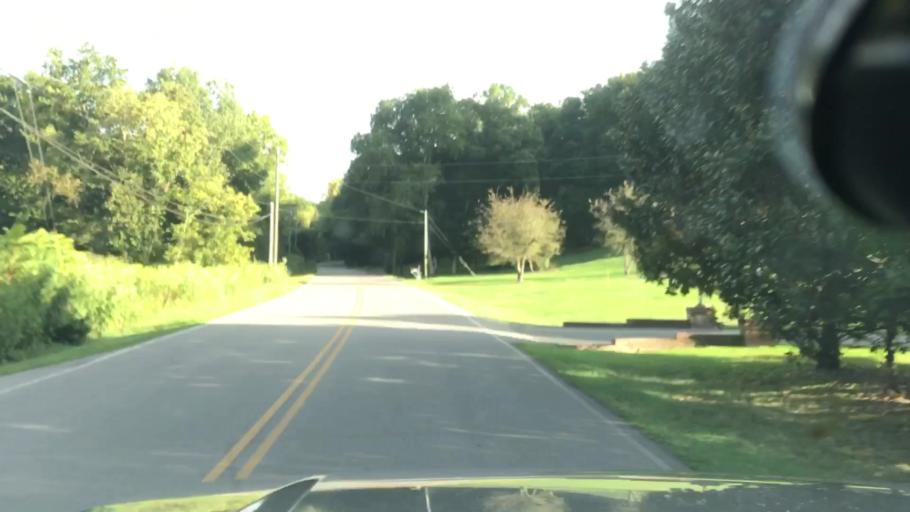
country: US
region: Tennessee
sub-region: Davidson County
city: Forest Hills
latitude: 36.0550
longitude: -86.8440
